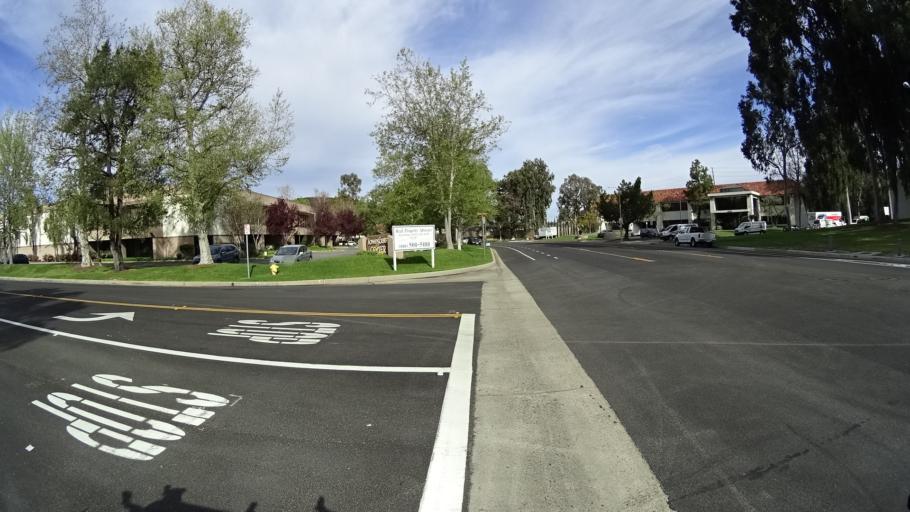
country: US
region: California
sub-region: Ventura County
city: Thousand Oaks
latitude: 34.1605
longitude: -118.8333
